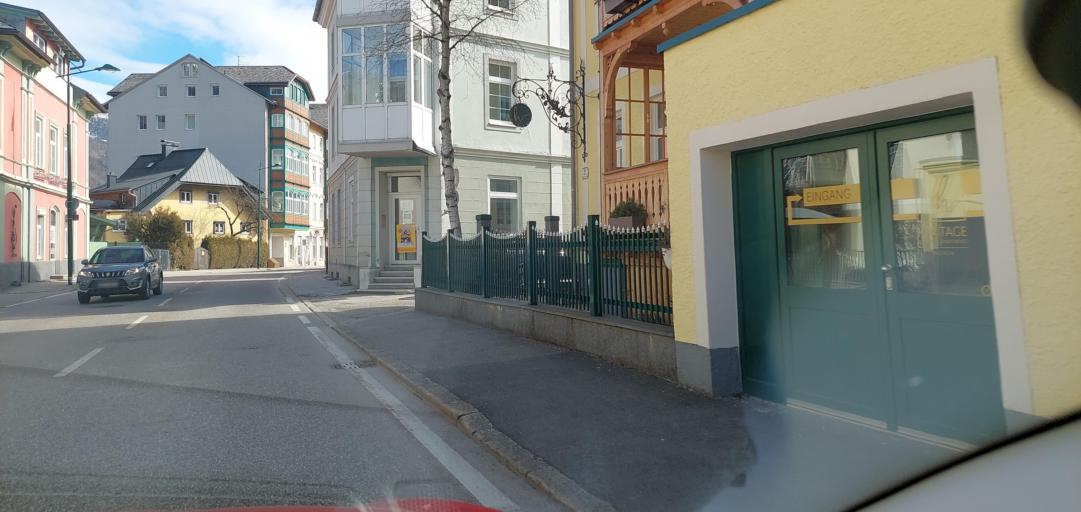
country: AT
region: Upper Austria
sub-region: Politischer Bezirk Gmunden
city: Bad Ischl
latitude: 47.7139
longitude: 13.6179
